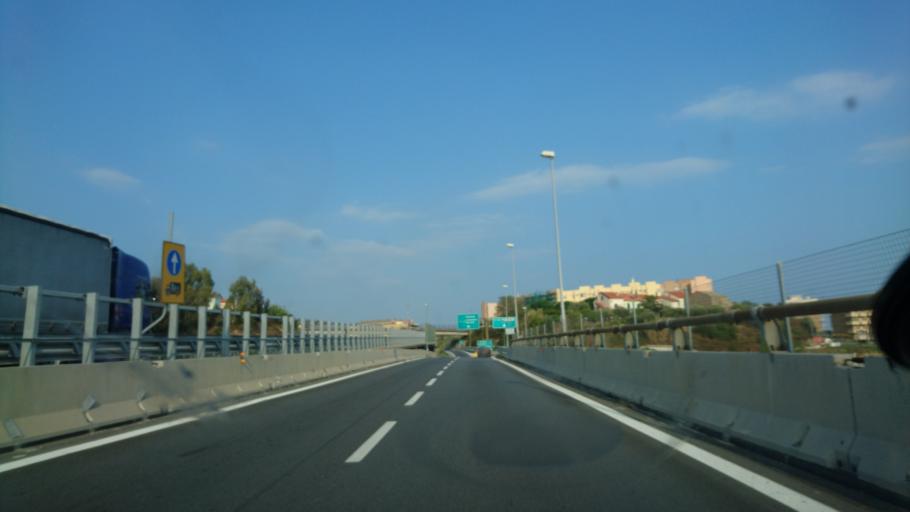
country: IT
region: Liguria
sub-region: Provincia di Savona
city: Valleggia
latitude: 44.2888
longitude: 8.4421
